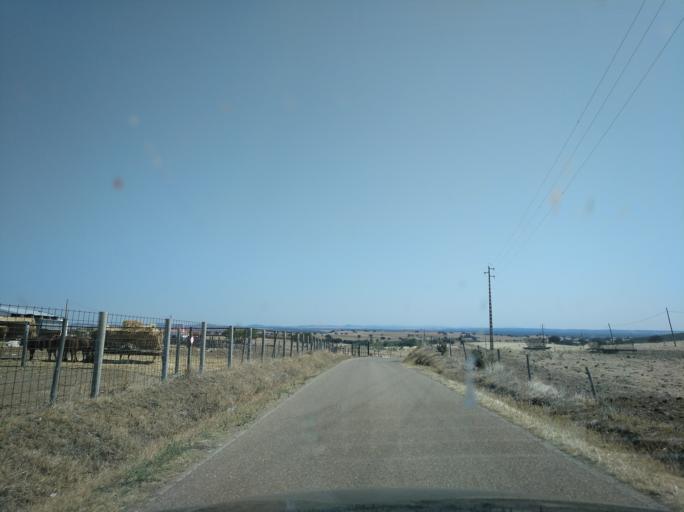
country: PT
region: Portalegre
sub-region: Campo Maior
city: Campo Maior
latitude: 39.0264
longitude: -7.0282
